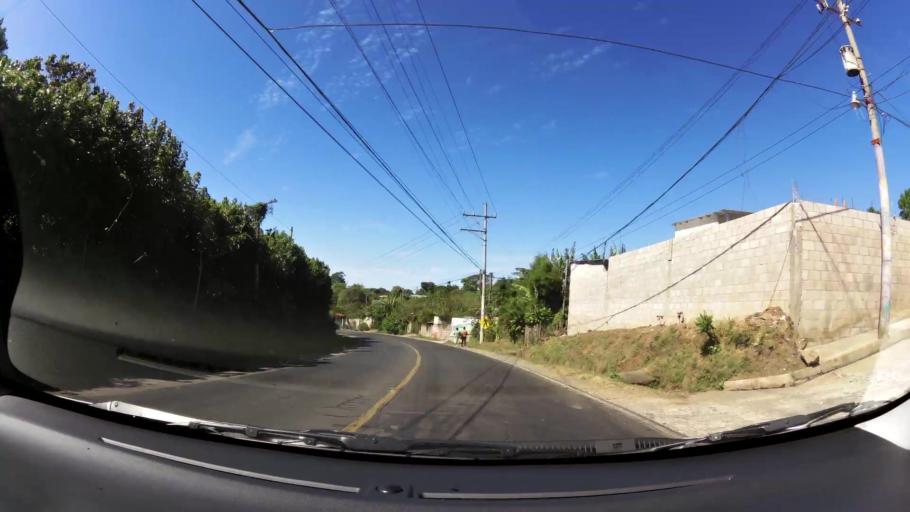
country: SV
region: Ahuachapan
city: Concepcion de Ataco
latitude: 13.8496
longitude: -89.8228
